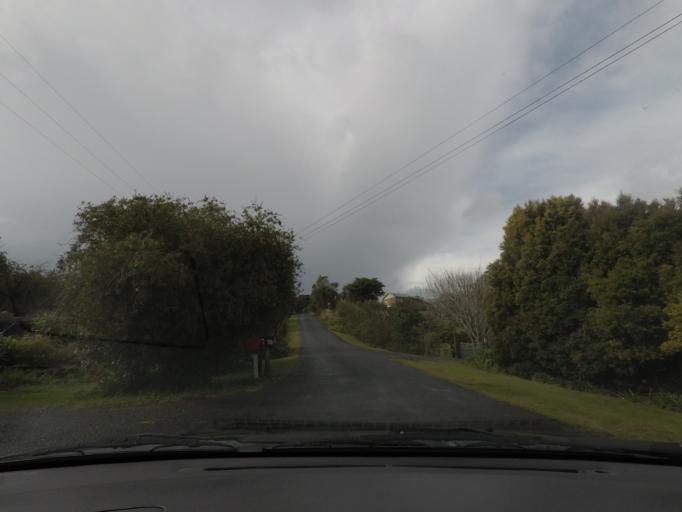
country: NZ
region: Auckland
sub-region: Auckland
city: Warkworth
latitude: -36.4716
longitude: 174.7328
